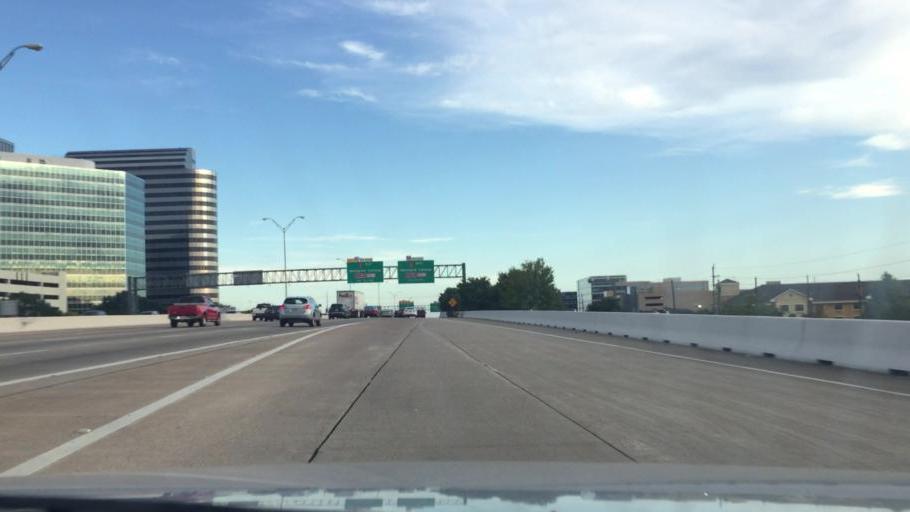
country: US
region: Texas
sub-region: Harris County
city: Bunker Hill Village
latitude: 29.7307
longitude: -95.5578
